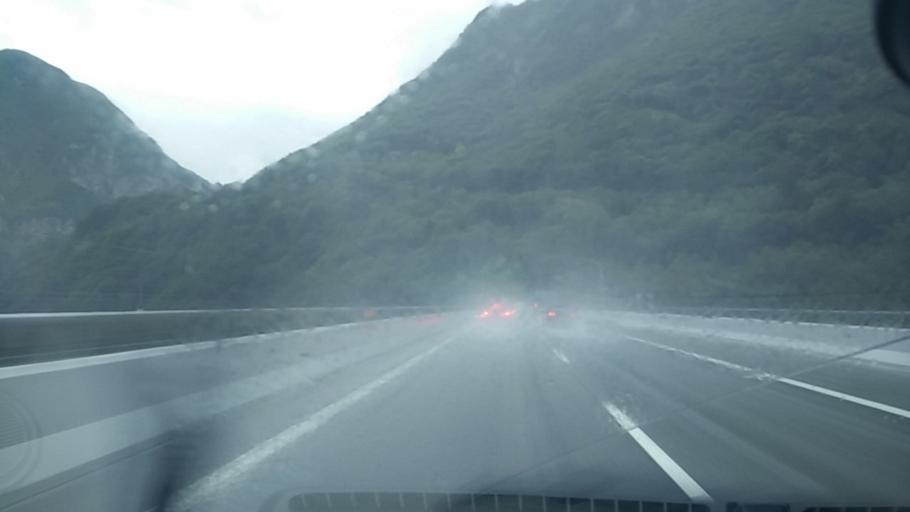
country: IT
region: Friuli Venezia Giulia
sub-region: Provincia di Udine
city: Dogna
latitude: 46.4595
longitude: 13.3038
